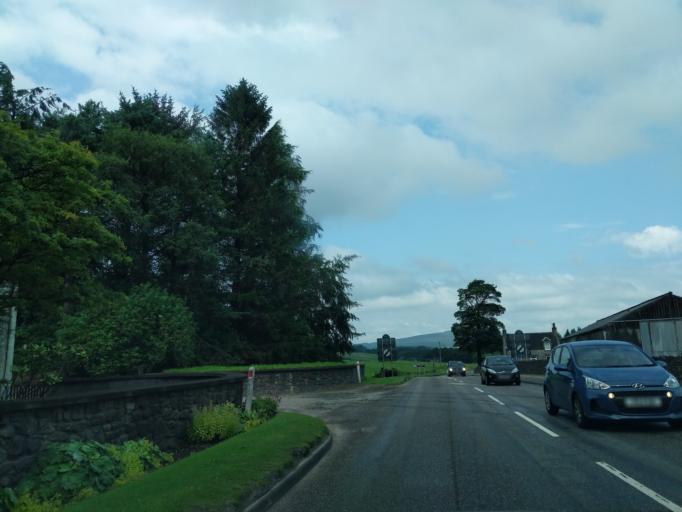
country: GB
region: Scotland
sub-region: Moray
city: Dufftown
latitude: 57.4555
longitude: -3.1311
